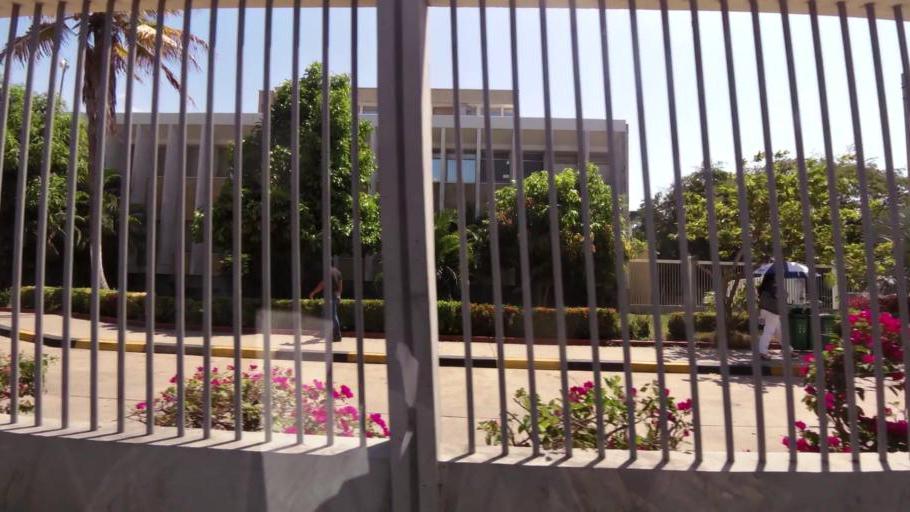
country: CO
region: Bolivar
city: Cartagena
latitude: 10.4094
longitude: -75.5344
